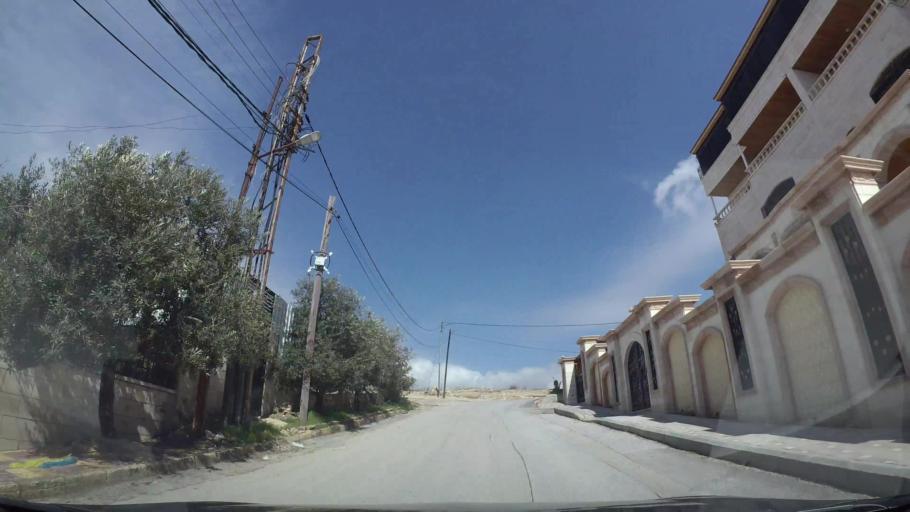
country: JO
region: Amman
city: Al Jubayhah
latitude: 31.9973
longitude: 35.9042
